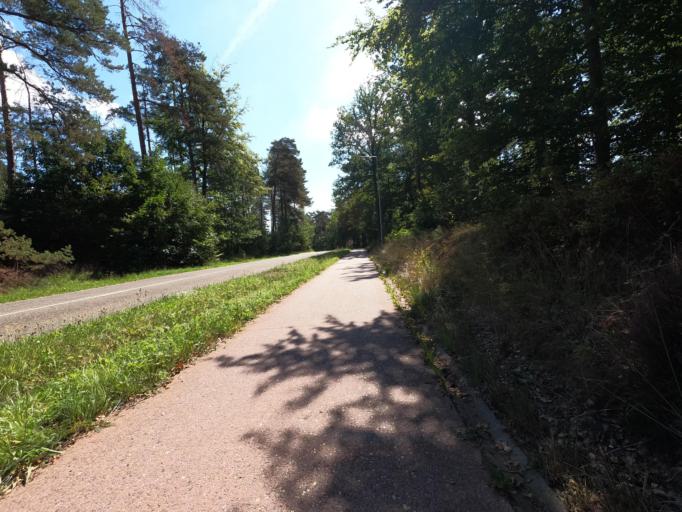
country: BE
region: Flanders
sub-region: Provincie Antwerpen
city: Westerlo
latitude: 51.0633
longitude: 4.9232
